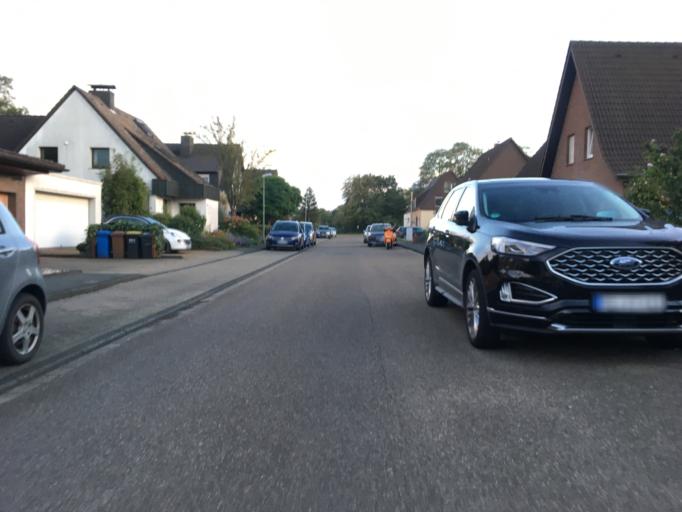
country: DE
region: North Rhine-Westphalia
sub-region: Regierungsbezirk Munster
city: Bottrop
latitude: 51.4934
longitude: 6.9215
